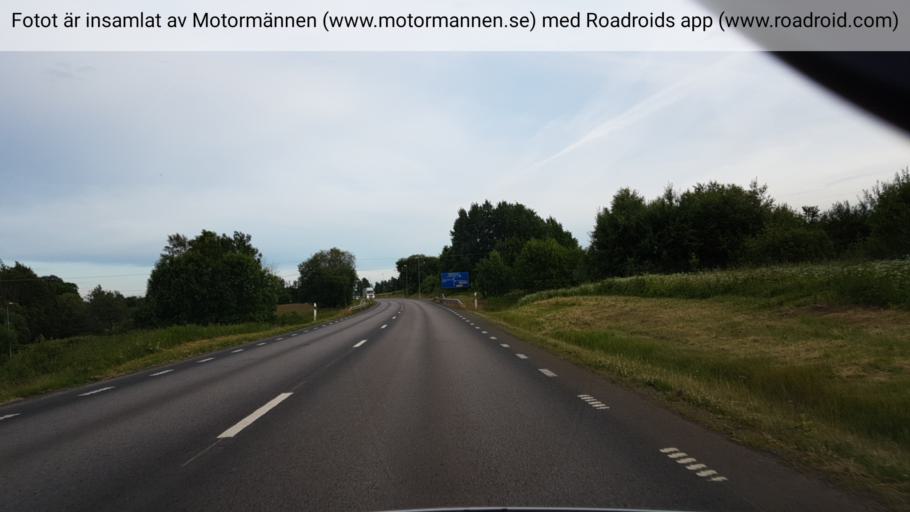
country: SE
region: Vaestra Goetaland
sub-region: Falkopings Kommun
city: Falkoeping
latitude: 58.1944
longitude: 13.5604
